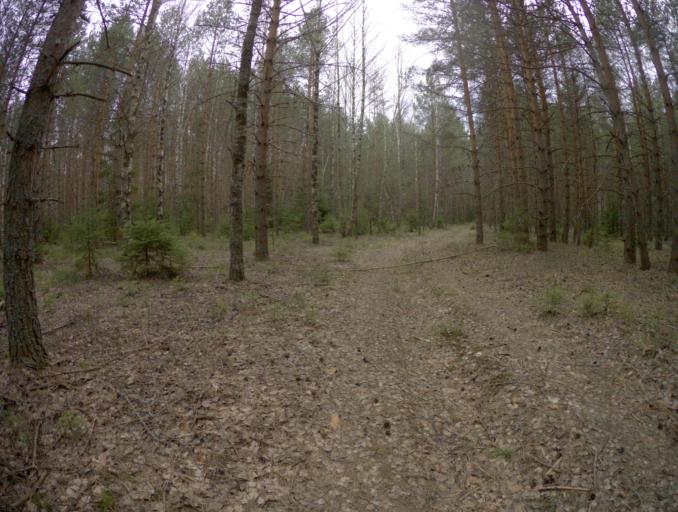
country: RU
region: Vladimir
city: Raduzhnyy
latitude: 55.9267
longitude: 40.2640
